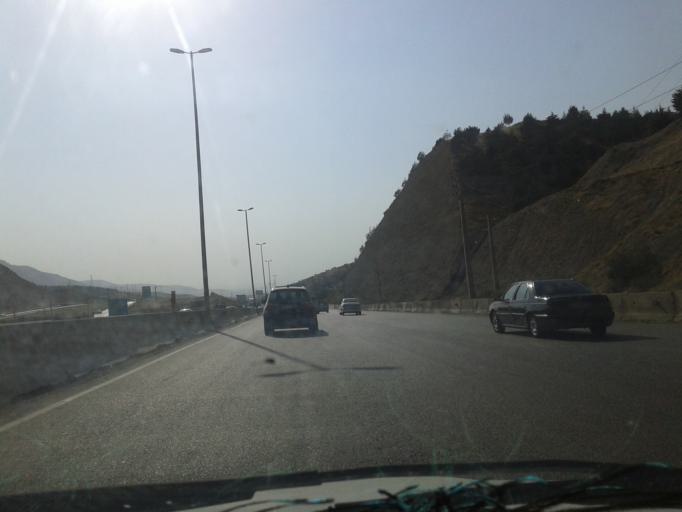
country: IR
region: Tehran
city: Tehran
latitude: 35.7332
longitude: 51.6558
